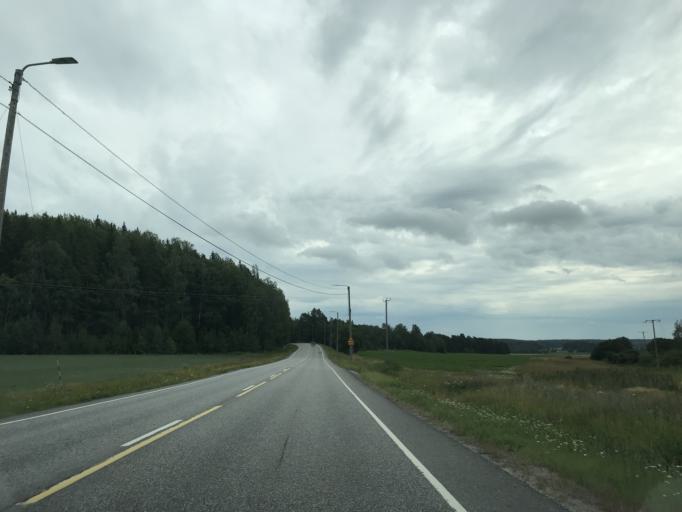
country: FI
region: Varsinais-Suomi
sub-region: Turku
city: Paimio
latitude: 60.4257
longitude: 22.6293
